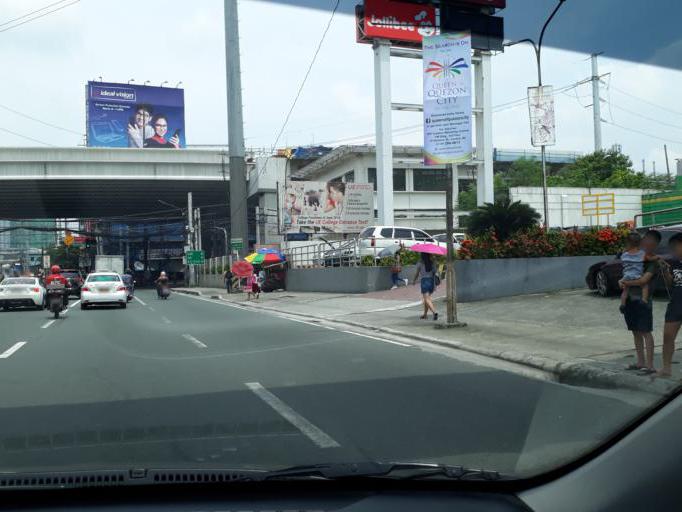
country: PH
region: Calabarzon
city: Del Monte
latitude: 14.6187
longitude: 121.0142
